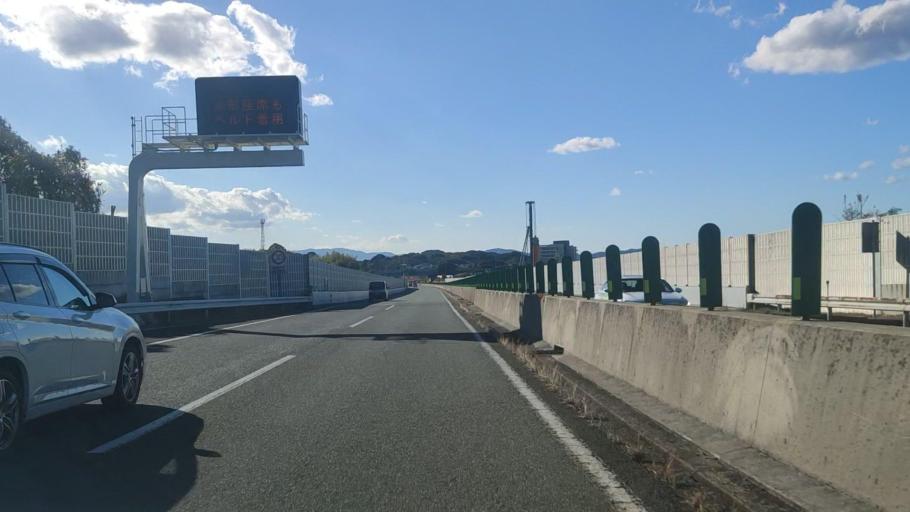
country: JP
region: Fukuoka
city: Nakama
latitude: 33.8195
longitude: 130.7552
